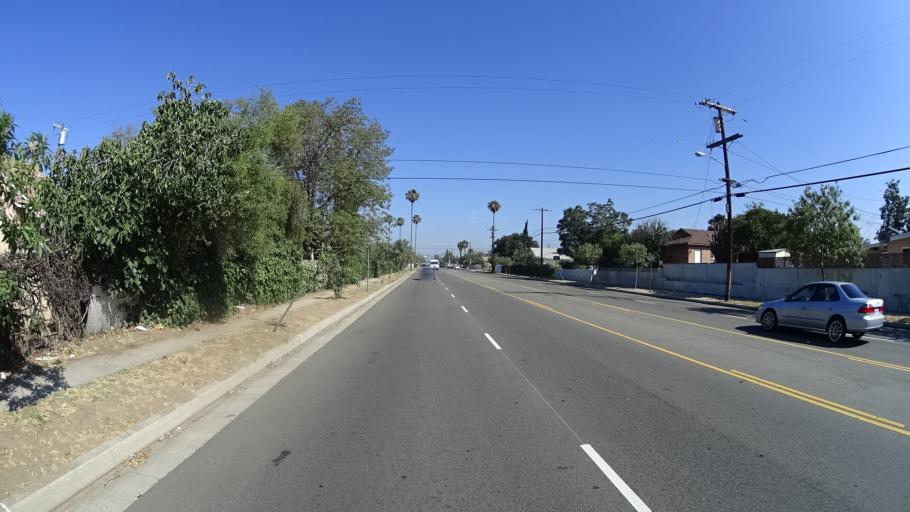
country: US
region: California
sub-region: Los Angeles County
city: San Fernando
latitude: 34.2345
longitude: -118.4182
